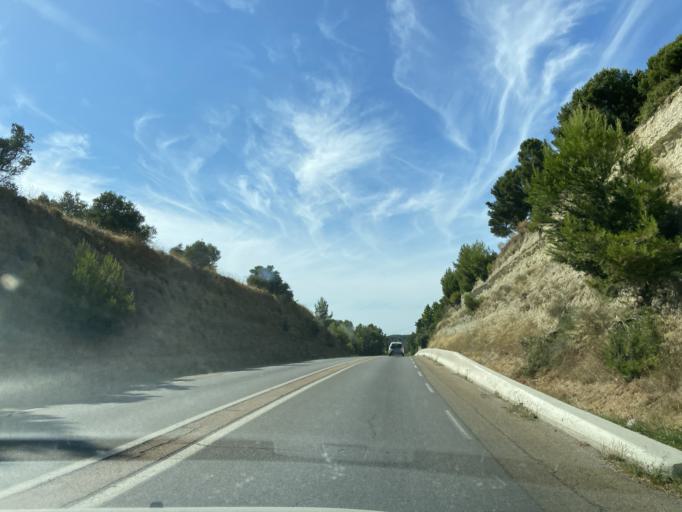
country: FR
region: Provence-Alpes-Cote d'Azur
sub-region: Departement des Bouches-du-Rhone
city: Saint-Chamas
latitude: 43.5518
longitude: 5.0372
